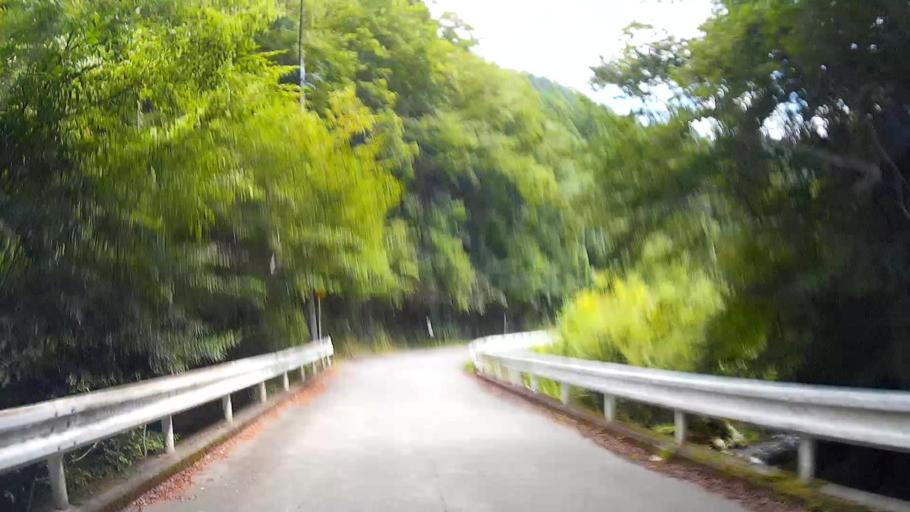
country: JP
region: Saitama
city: Chichibu
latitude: 35.9090
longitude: 139.0914
